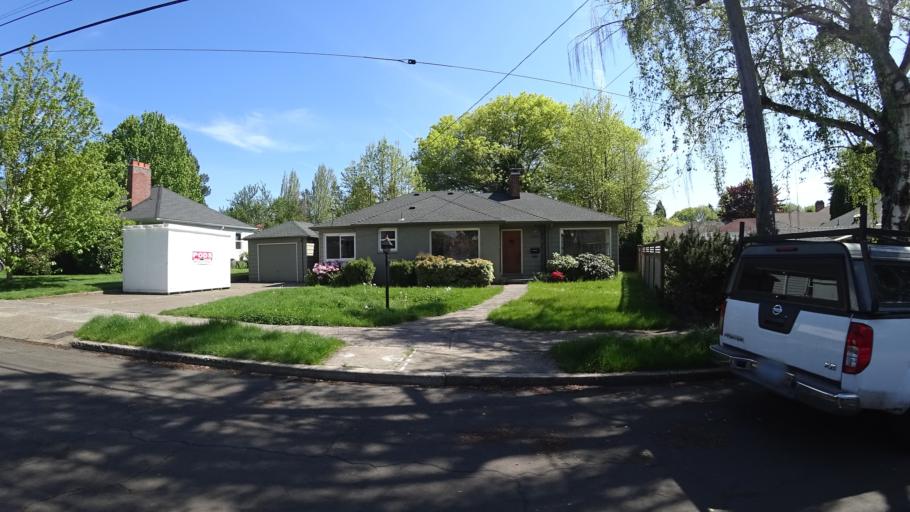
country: US
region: Oregon
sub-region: Clackamas County
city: Milwaukie
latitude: 45.4835
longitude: -122.6287
